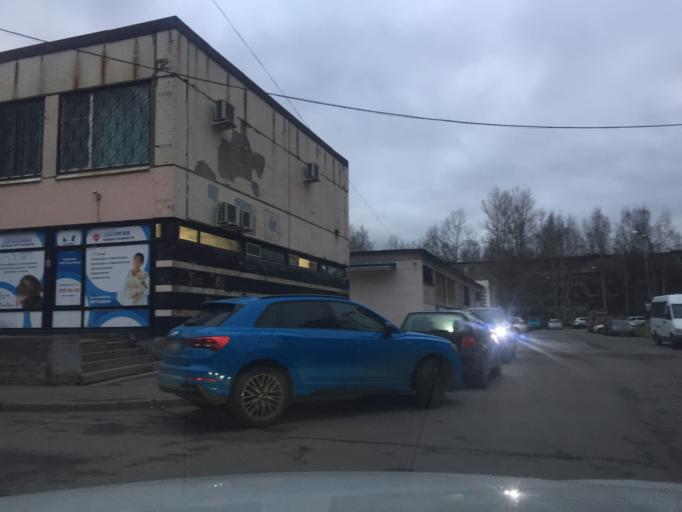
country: RU
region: St.-Petersburg
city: Grazhdanka
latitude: 60.0284
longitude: 30.4061
